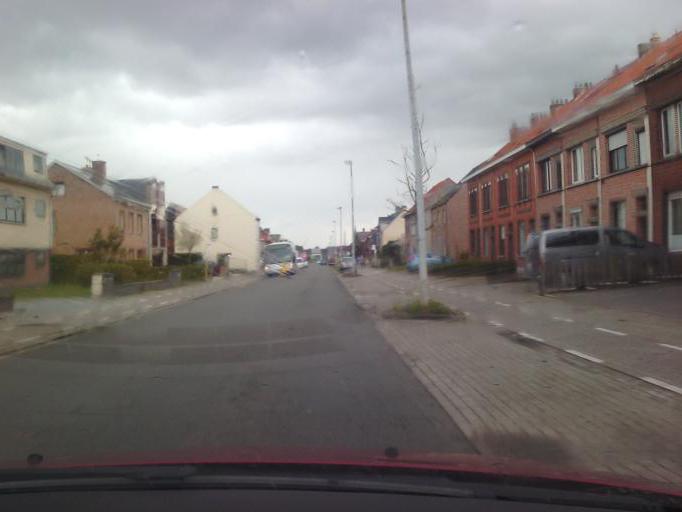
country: BE
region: Flanders
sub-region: Provincie Oost-Vlaanderen
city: Sint-Niklaas
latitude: 51.1441
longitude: 4.1478
